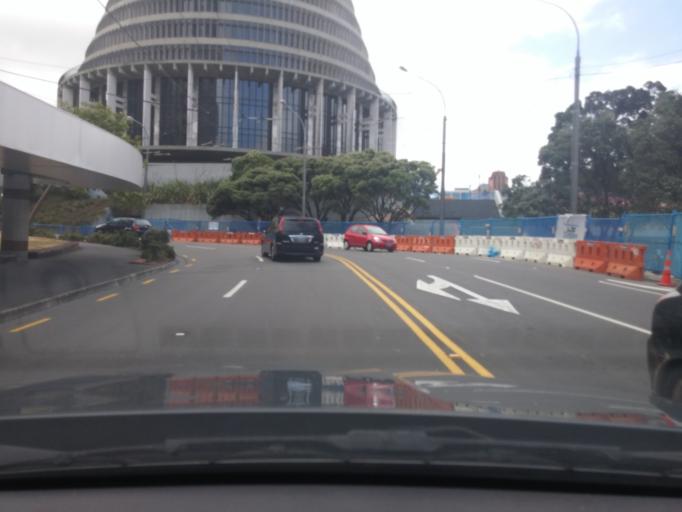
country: NZ
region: Wellington
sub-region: Wellington City
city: Wellington
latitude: -41.2793
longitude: 174.7769
